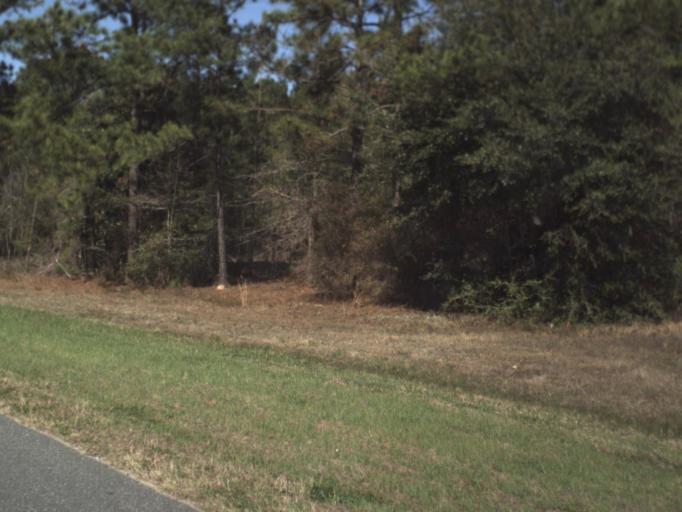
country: US
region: Florida
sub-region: Jackson County
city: Marianna
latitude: 30.7450
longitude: -85.1640
